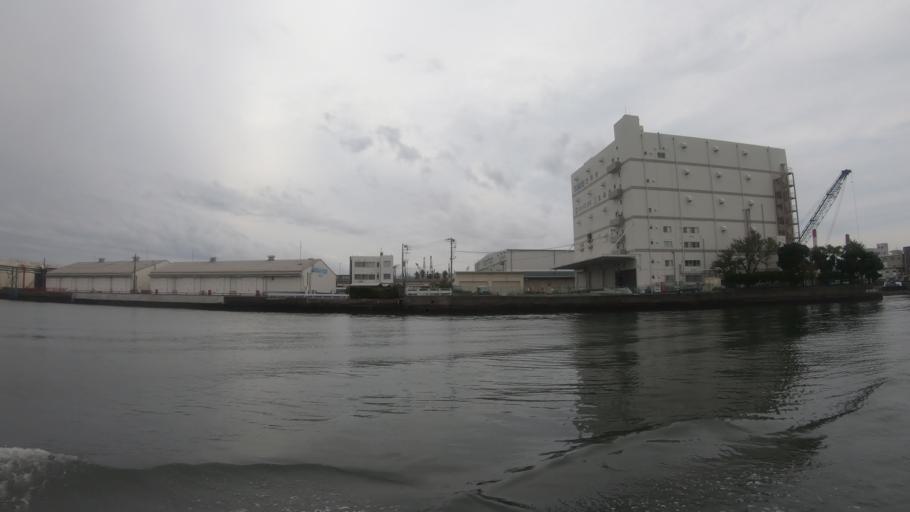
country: JP
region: Kanagawa
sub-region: Kawasaki-shi
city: Kawasaki
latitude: 35.4909
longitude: 139.6780
